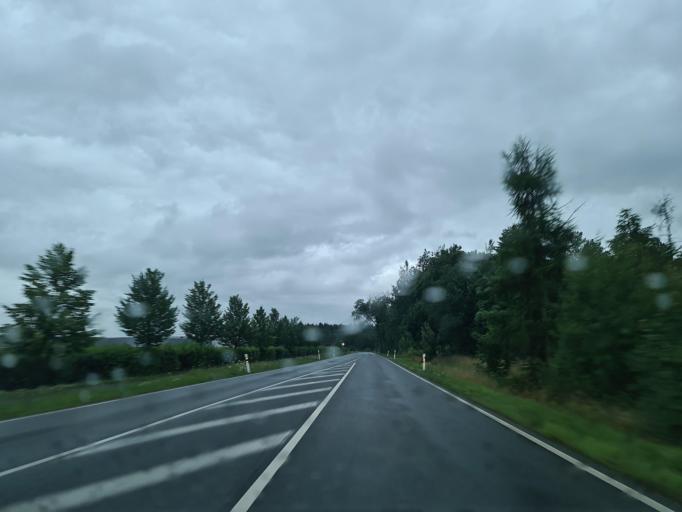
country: DE
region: Saxony
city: Limbach
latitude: 50.5512
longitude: 12.2651
